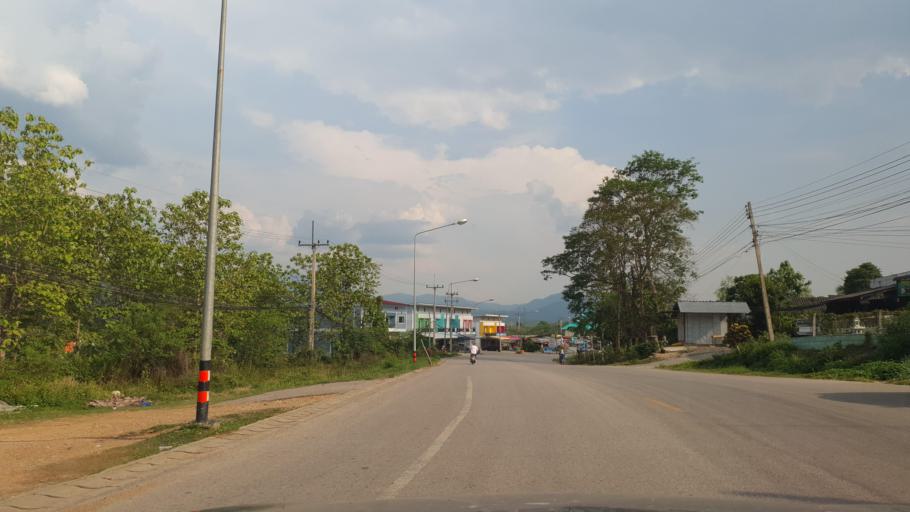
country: TH
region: Chiang Mai
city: Pai
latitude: 19.3527
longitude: 98.4349
